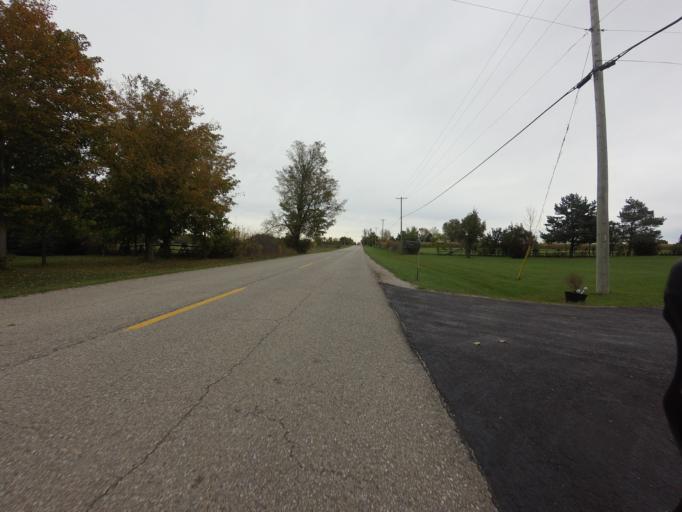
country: CA
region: Ontario
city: Brockville
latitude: 44.6761
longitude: -75.8628
